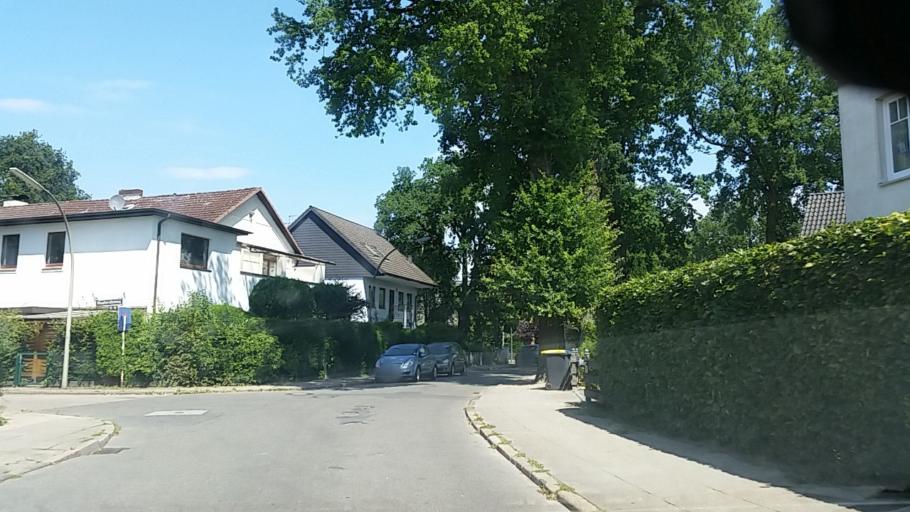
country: DE
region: Schleswig-Holstein
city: Wedel
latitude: 53.5798
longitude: 9.7615
